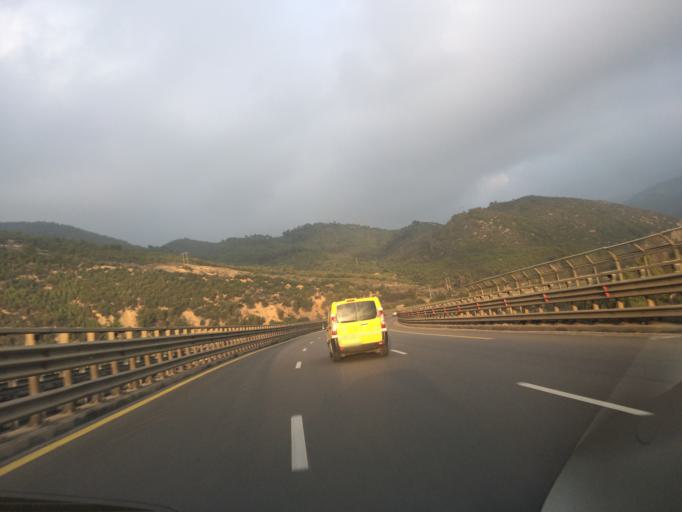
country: DZ
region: Tipaza
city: El Affroun
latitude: 36.4014
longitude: 2.5395
